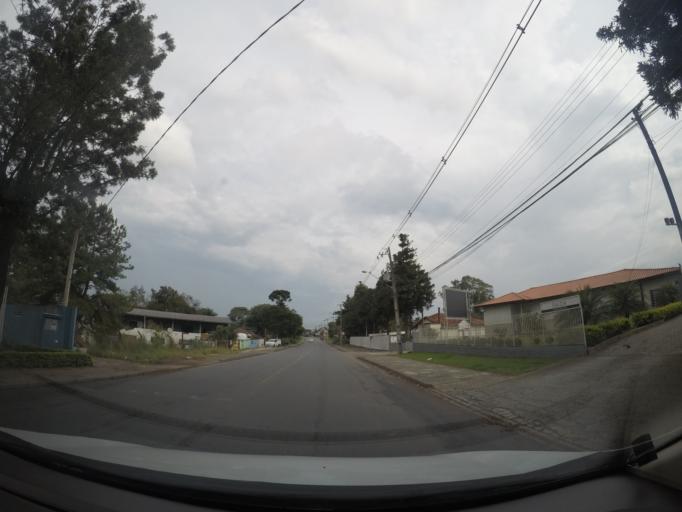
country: BR
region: Parana
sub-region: Sao Jose Dos Pinhais
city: Sao Jose dos Pinhais
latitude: -25.5141
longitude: -49.2608
